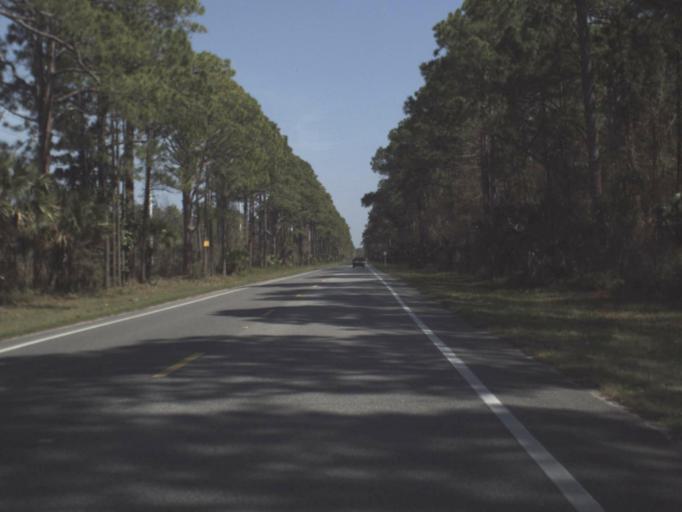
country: US
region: Florida
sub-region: Franklin County
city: Apalachicola
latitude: 29.7158
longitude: -85.0369
